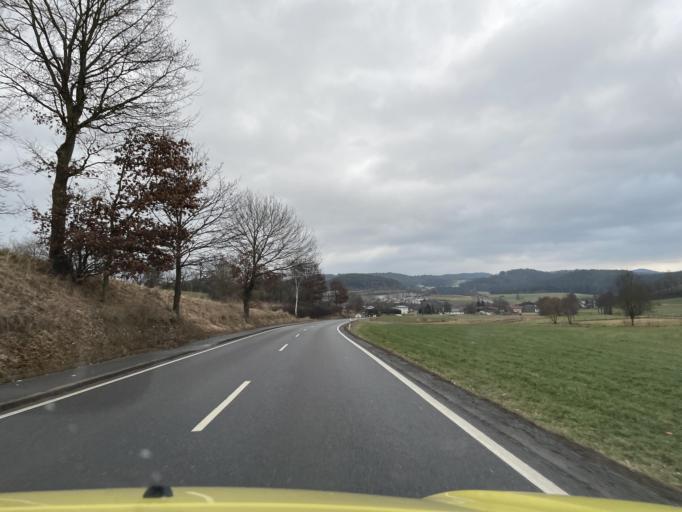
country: DE
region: Bavaria
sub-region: Upper Palatinate
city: Miltach
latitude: 49.1565
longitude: 12.7541
